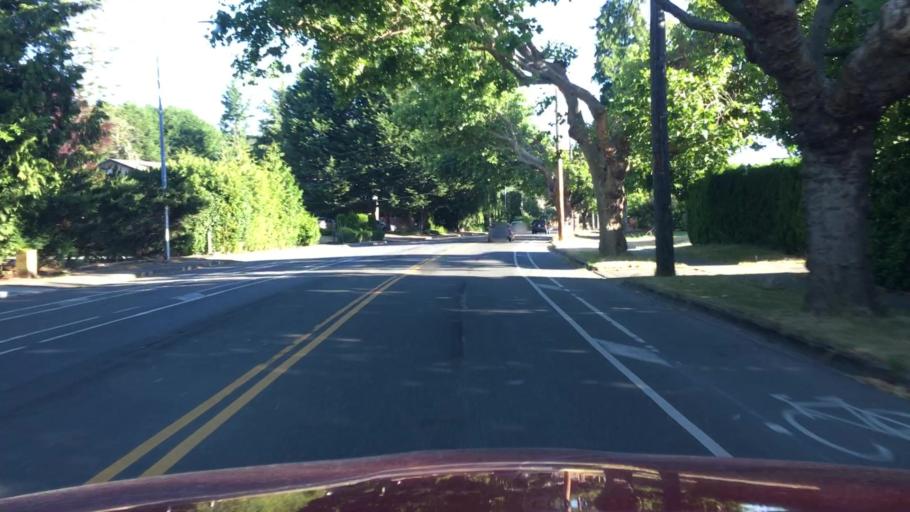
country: CA
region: British Columbia
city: Oak Bay
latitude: 48.4803
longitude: -123.3358
